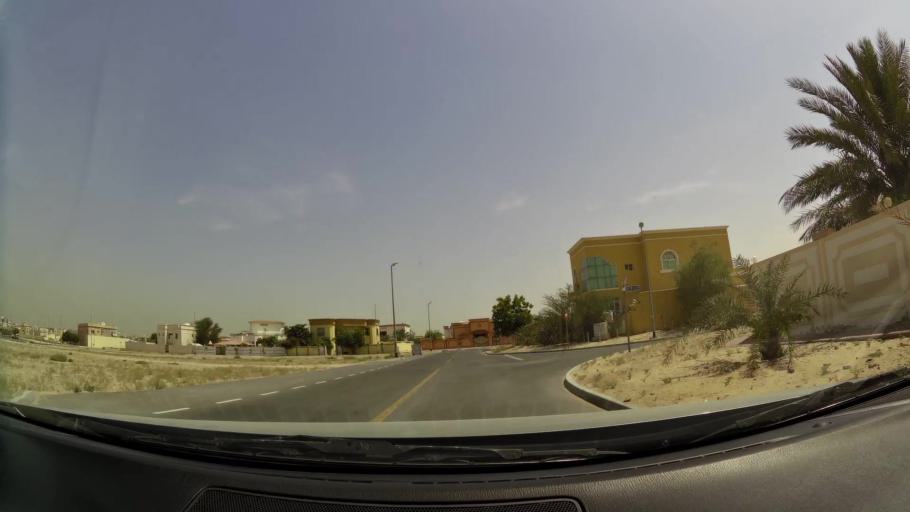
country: AE
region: Ash Shariqah
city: Sharjah
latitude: 25.1794
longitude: 55.4186
